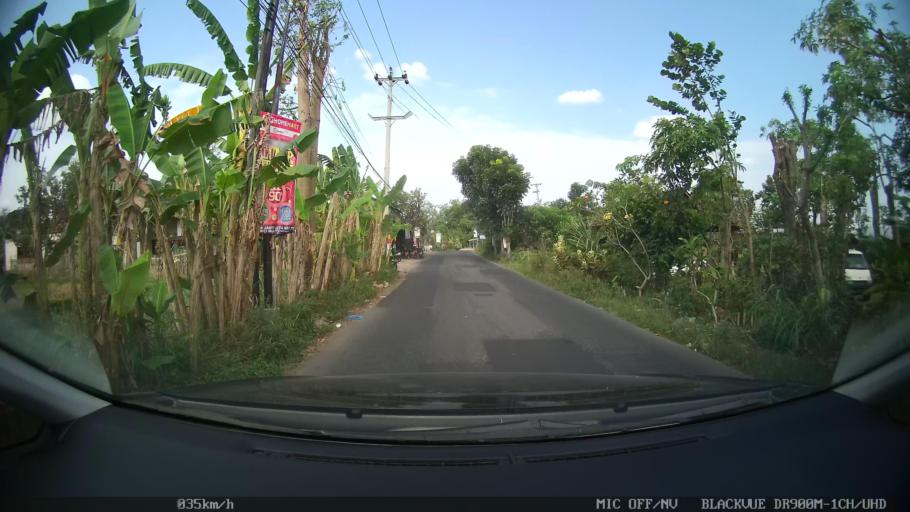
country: ID
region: Daerah Istimewa Yogyakarta
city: Melati
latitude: -7.7300
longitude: 110.4059
